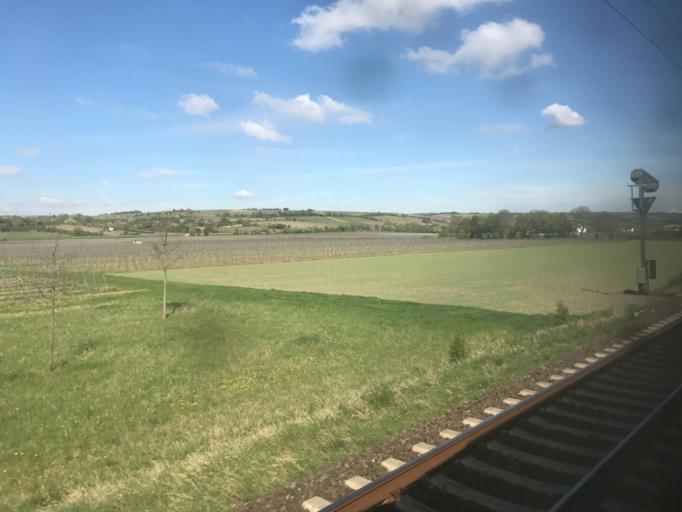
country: DE
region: Rheinland-Pfalz
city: Guntersblum
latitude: 49.8043
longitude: 8.3523
